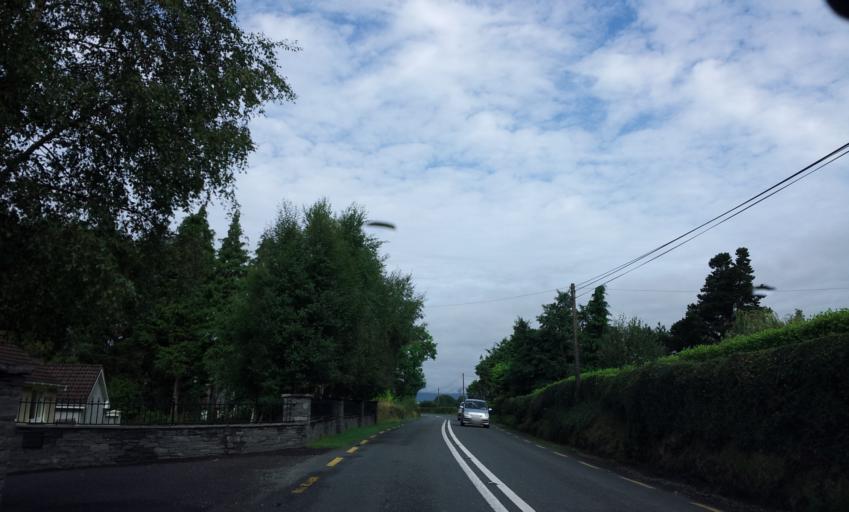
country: IE
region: Munster
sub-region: Ciarrai
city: Killorglin
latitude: 52.0780
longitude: -9.6590
